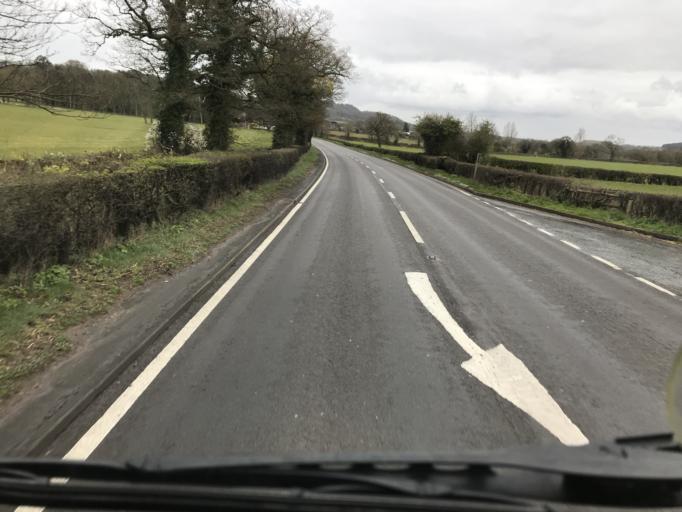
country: GB
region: England
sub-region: Cheshire West and Chester
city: Tattenhall
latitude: 53.1032
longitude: -2.7781
